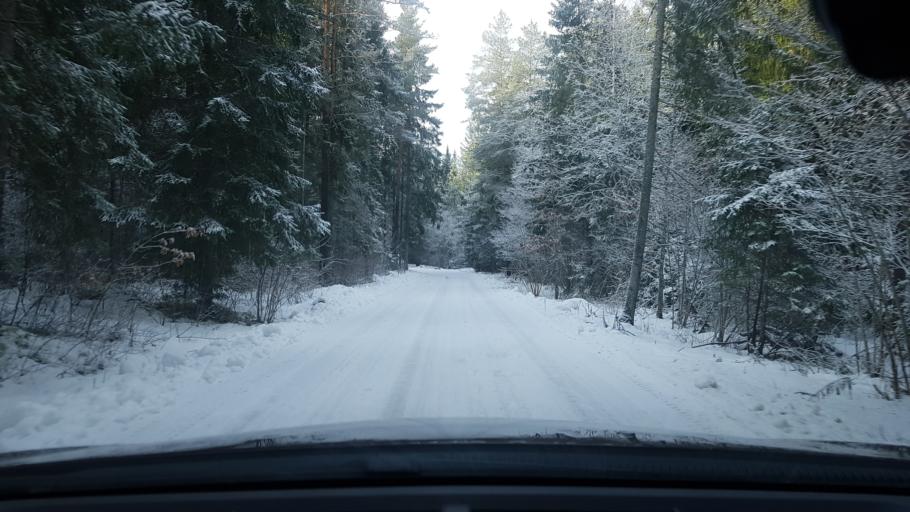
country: EE
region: Harju
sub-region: Keila linn
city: Keila
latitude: 59.2931
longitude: 24.2586
